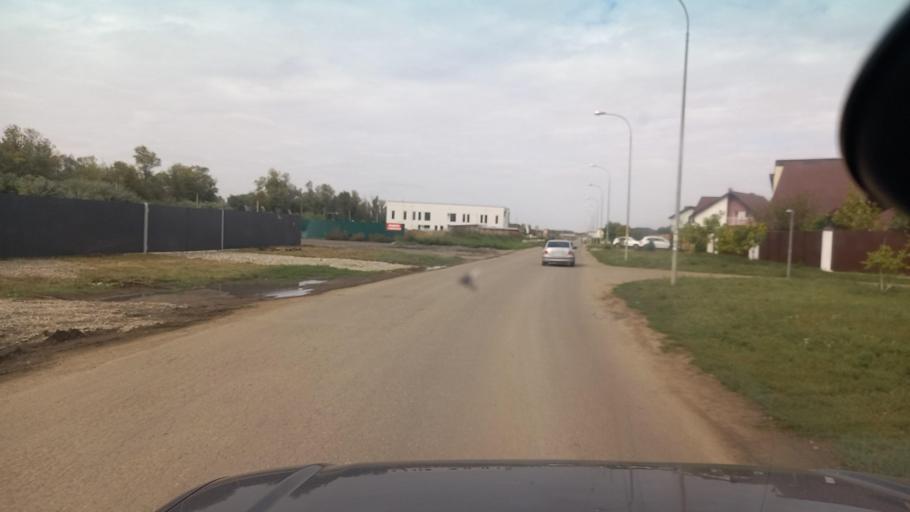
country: RU
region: Krasnodarskiy
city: Krasnodar
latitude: 45.1172
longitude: 38.9186
